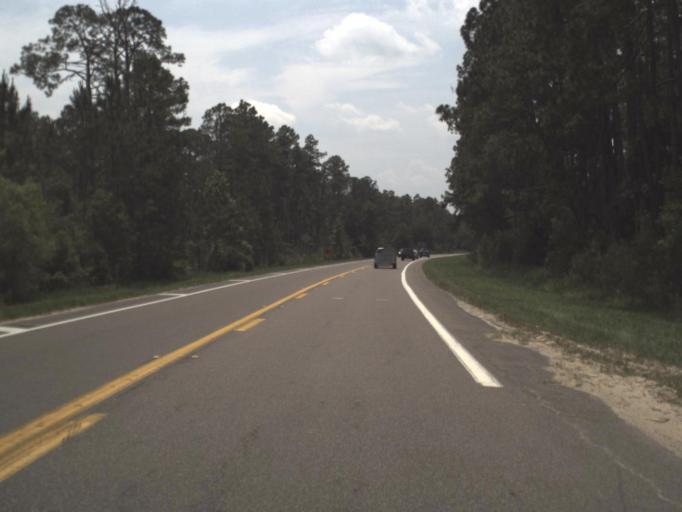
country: US
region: Florida
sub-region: Putnam County
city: Palatka
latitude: 29.4741
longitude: -81.7390
